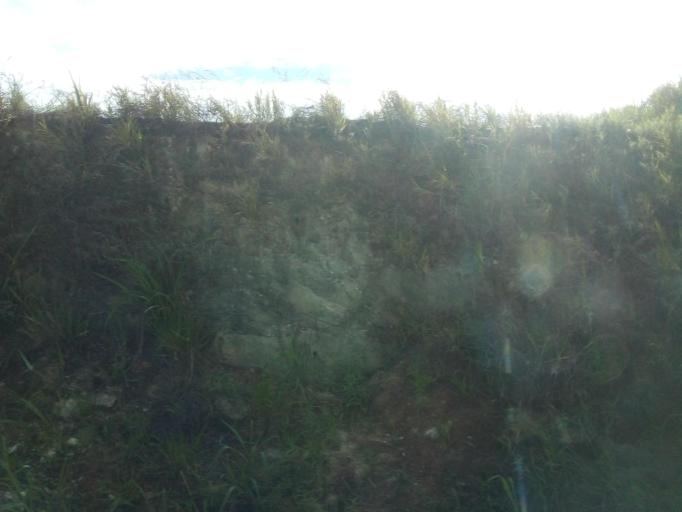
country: BR
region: Minas Gerais
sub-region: Belo Horizonte
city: Belo Horizonte
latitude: -19.8878
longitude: -43.8634
